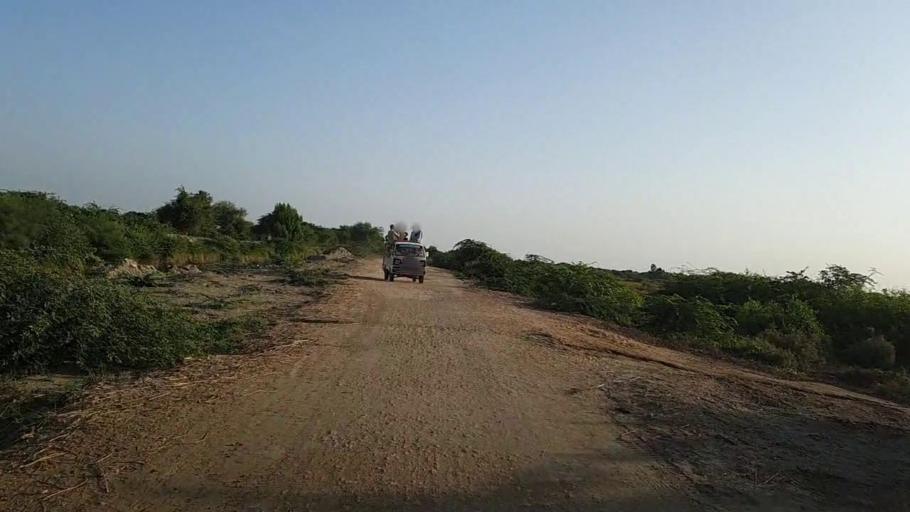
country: PK
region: Sindh
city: Kario
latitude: 24.7179
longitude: 68.6673
